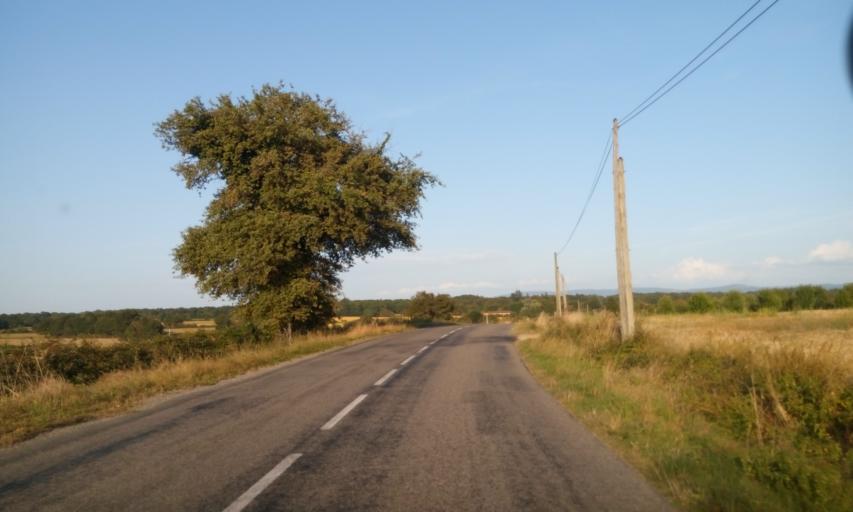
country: FR
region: Rhone-Alpes
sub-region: Departement de l'Ain
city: Chatillon-la-Palud
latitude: 46.0244
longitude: 5.2316
